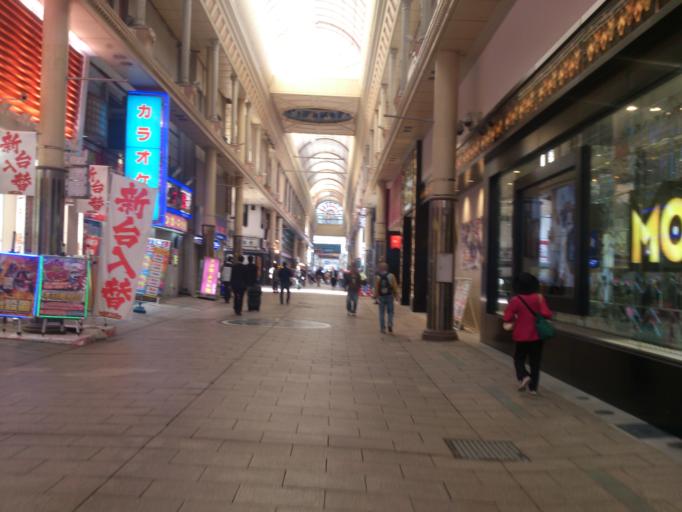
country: JP
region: Kagoshima
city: Kagoshima-shi
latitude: 31.5892
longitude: 130.5561
